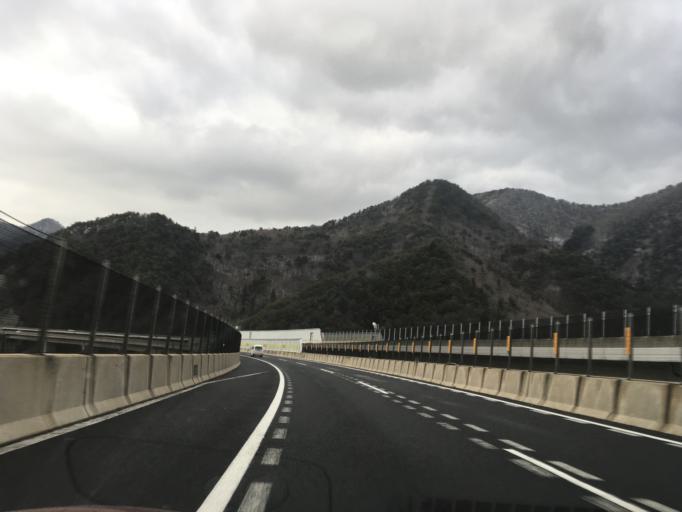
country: JP
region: Yamagata
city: Yamagata-shi
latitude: 38.2341
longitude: 140.4098
